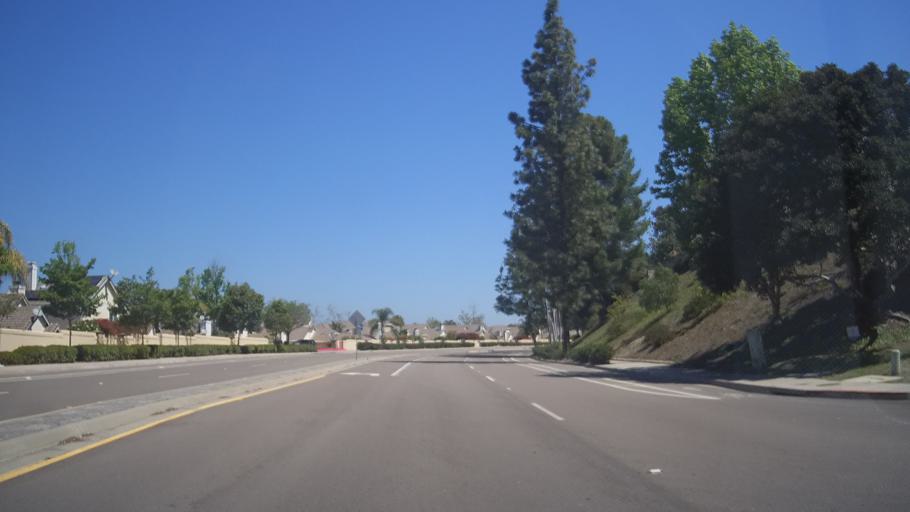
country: US
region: California
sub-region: San Diego County
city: Poway
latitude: 32.9681
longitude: -117.0893
